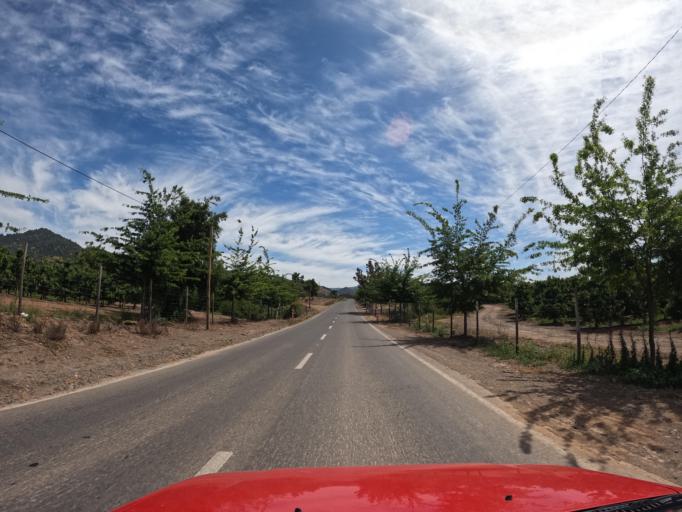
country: CL
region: Maule
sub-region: Provincia de Talca
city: Talca
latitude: -35.1219
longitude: -71.6642
